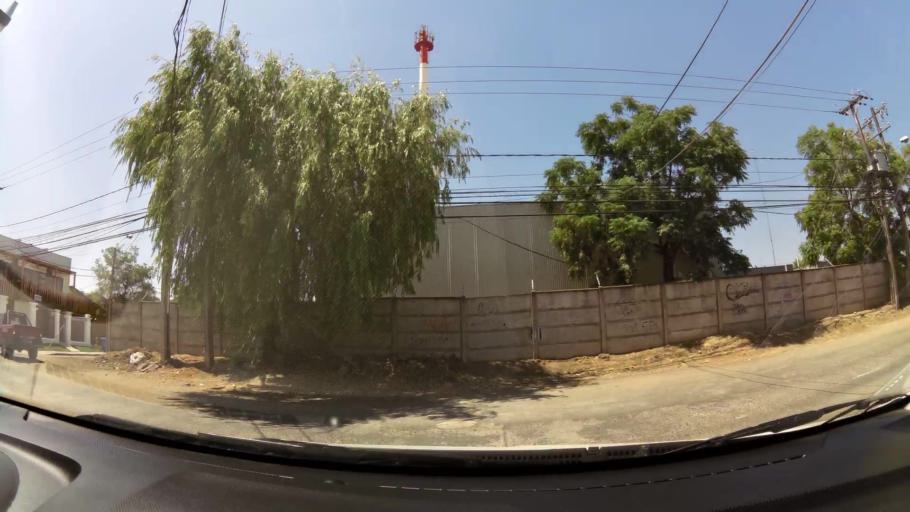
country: CL
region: Maule
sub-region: Provincia de Talca
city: Talca
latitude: -35.4314
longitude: -71.6325
